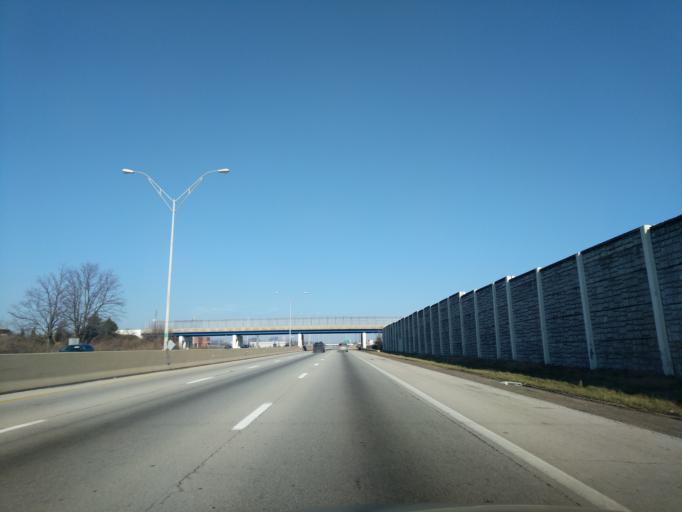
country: US
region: Ohio
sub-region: Montgomery County
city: Northridge
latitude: 39.8118
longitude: -84.1888
